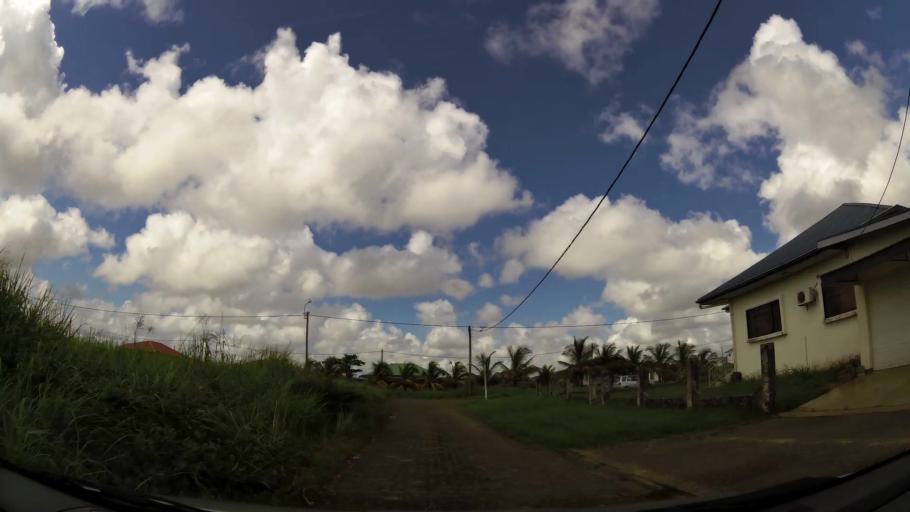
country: SR
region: Commewijne
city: Nieuw Amsterdam
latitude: 5.8677
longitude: -55.1220
